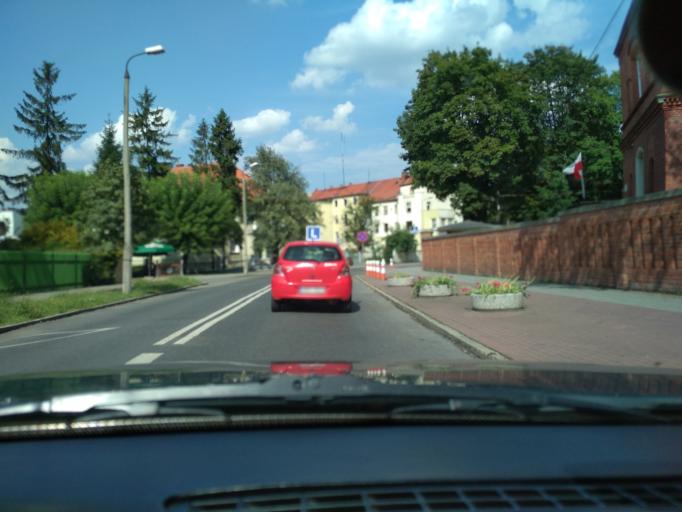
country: PL
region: Silesian Voivodeship
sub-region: Powiat raciborski
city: Raciborz
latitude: 50.0930
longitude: 18.2130
